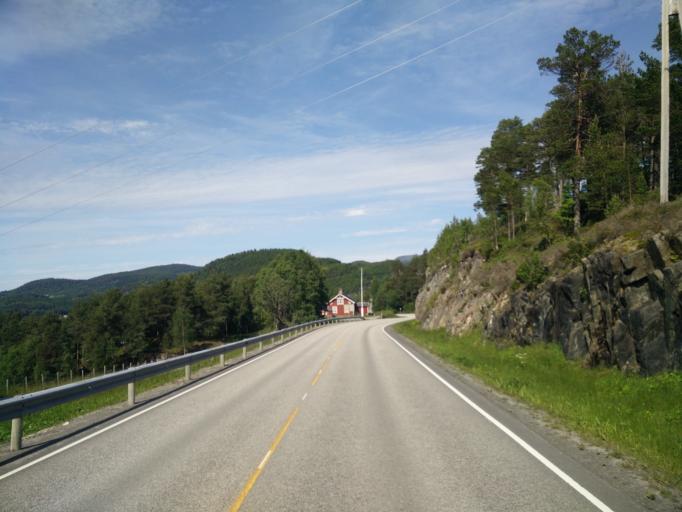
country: NO
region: More og Romsdal
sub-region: Kristiansund
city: Rensvik
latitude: 63.0124
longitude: 8.0012
